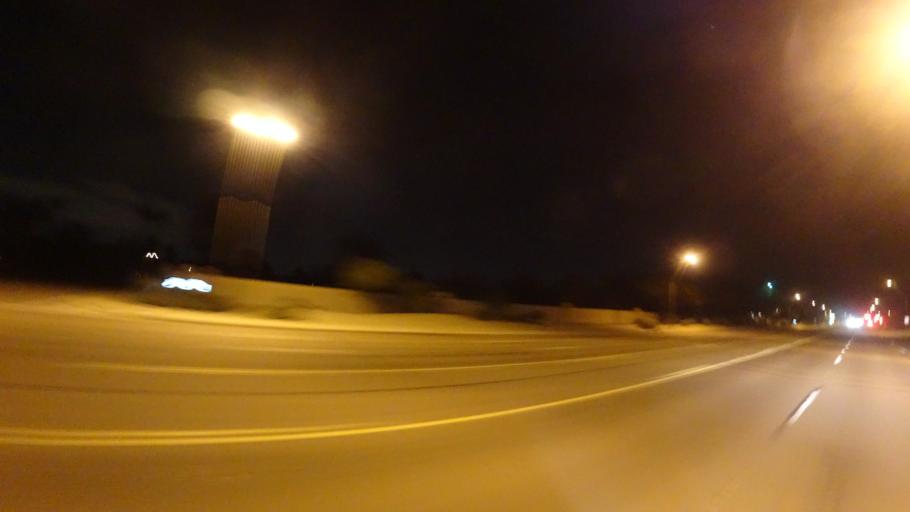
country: US
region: Arizona
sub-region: Maricopa County
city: Guadalupe
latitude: 33.3381
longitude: -111.9284
